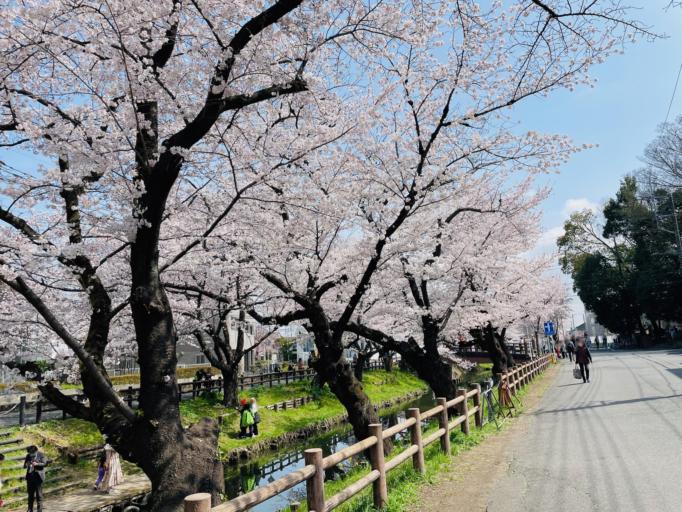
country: JP
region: Saitama
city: Kawagoe
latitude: 35.9283
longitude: 139.4880
